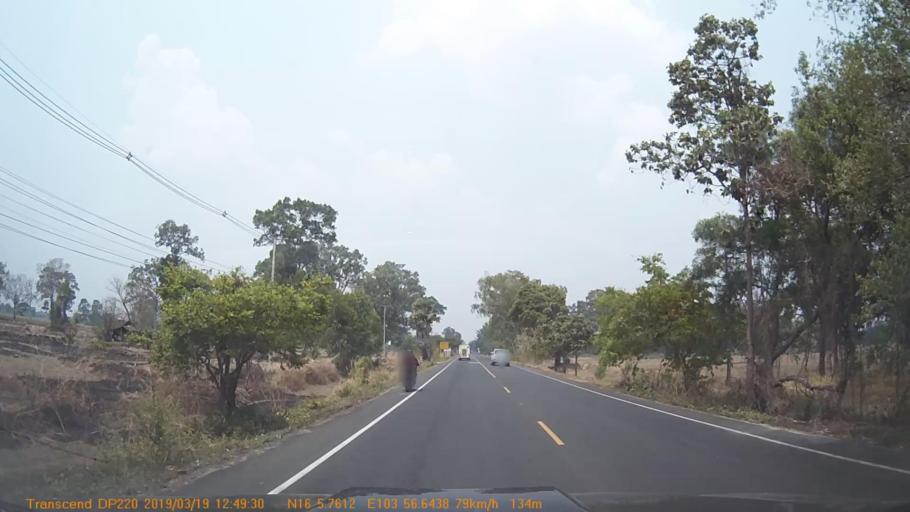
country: TH
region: Roi Et
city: Selaphum
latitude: 16.0965
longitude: 103.9441
